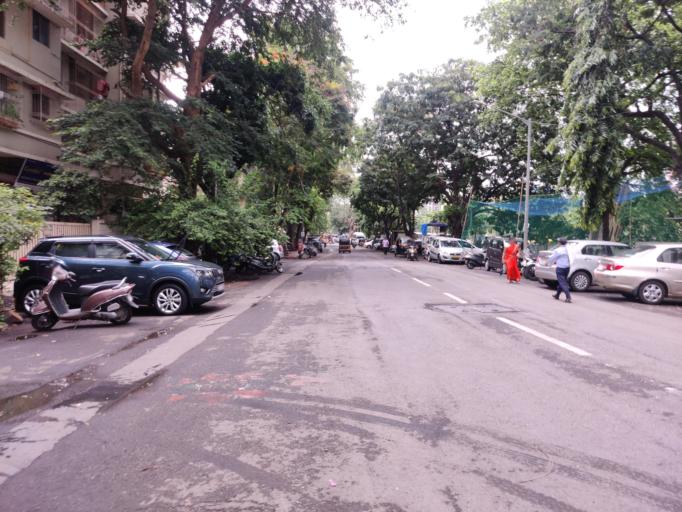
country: IN
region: Maharashtra
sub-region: Mumbai Suburban
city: Borivli
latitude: 19.2539
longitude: 72.8567
